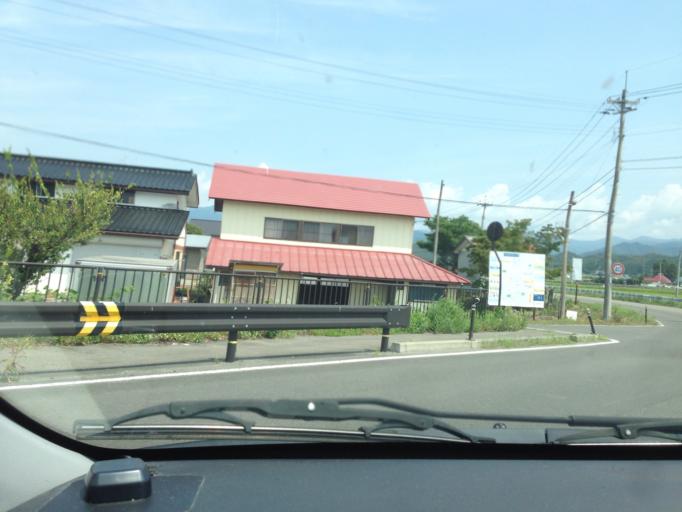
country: JP
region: Fukushima
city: Kitakata
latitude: 37.6744
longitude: 139.8803
